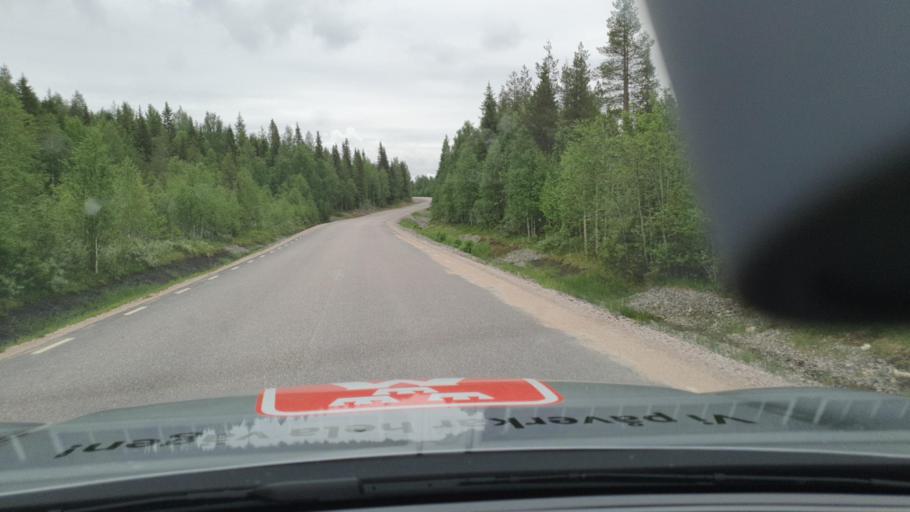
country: SE
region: Norrbotten
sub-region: Overtornea Kommun
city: OEvertornea
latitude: 66.5179
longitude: 23.3782
